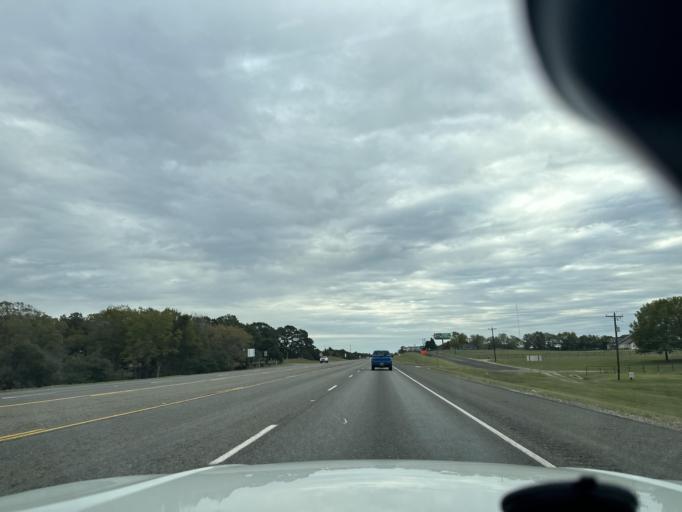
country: US
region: Texas
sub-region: Washington County
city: Brenham
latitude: 30.1787
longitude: -96.4698
